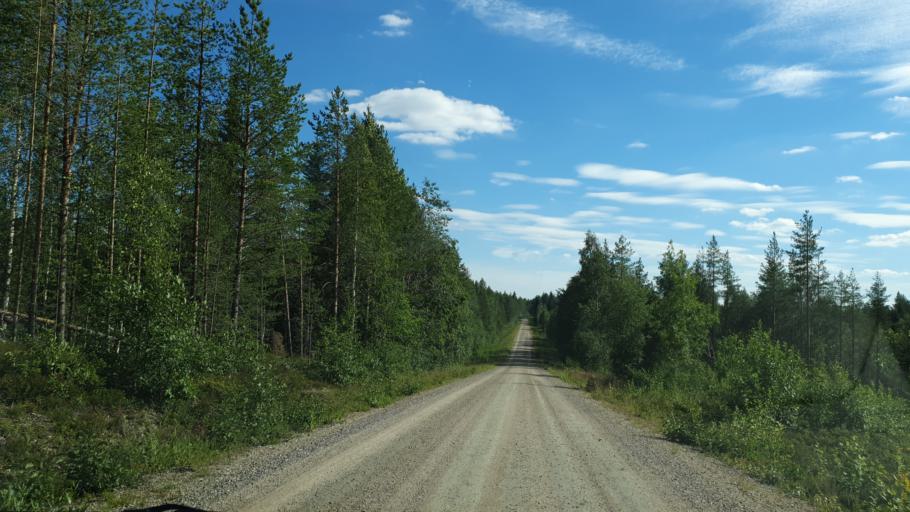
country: FI
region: Kainuu
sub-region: Kehys-Kainuu
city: Kuhmo
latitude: 64.1538
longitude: 29.3279
